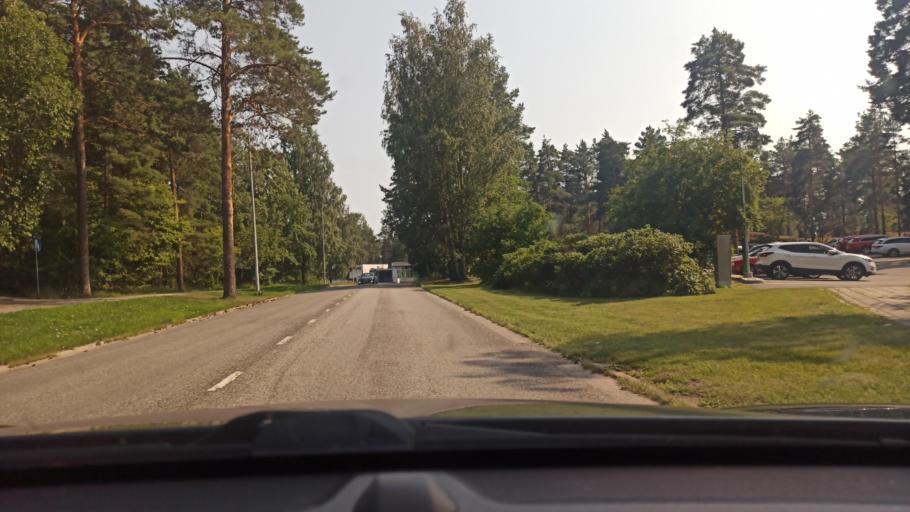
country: FI
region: Varsinais-Suomi
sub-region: Turku
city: Turku
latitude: 60.4624
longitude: 22.2181
